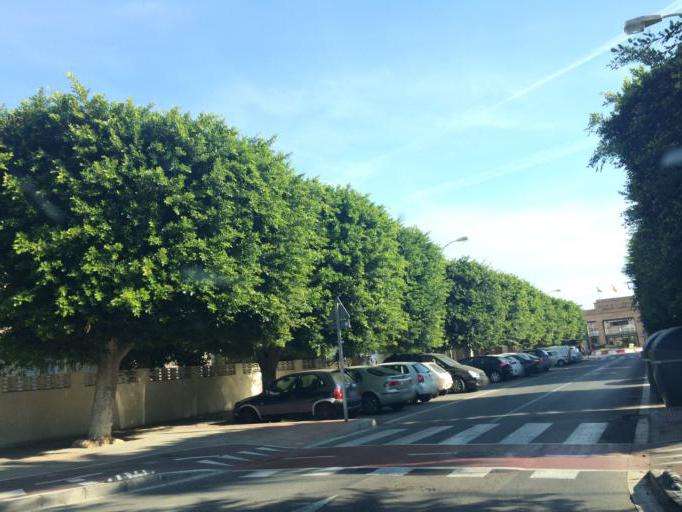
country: ES
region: Andalusia
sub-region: Provincia de Almeria
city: Almeria
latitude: 36.8307
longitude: -2.4504
